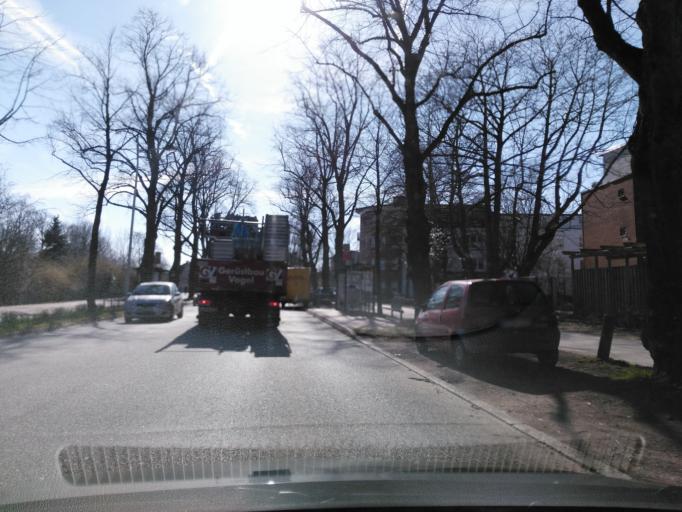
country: DE
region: Schleswig-Holstein
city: Kiel
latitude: 54.3067
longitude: 10.1092
